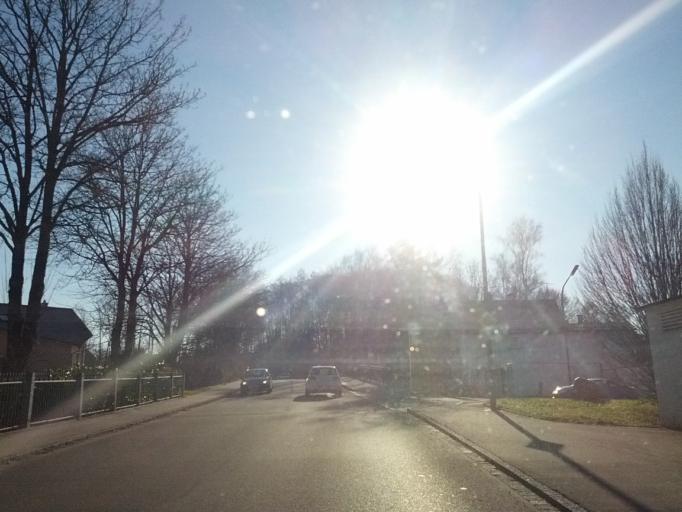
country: DE
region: Bavaria
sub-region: Swabia
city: Buxheim
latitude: 47.9970
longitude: 10.1347
